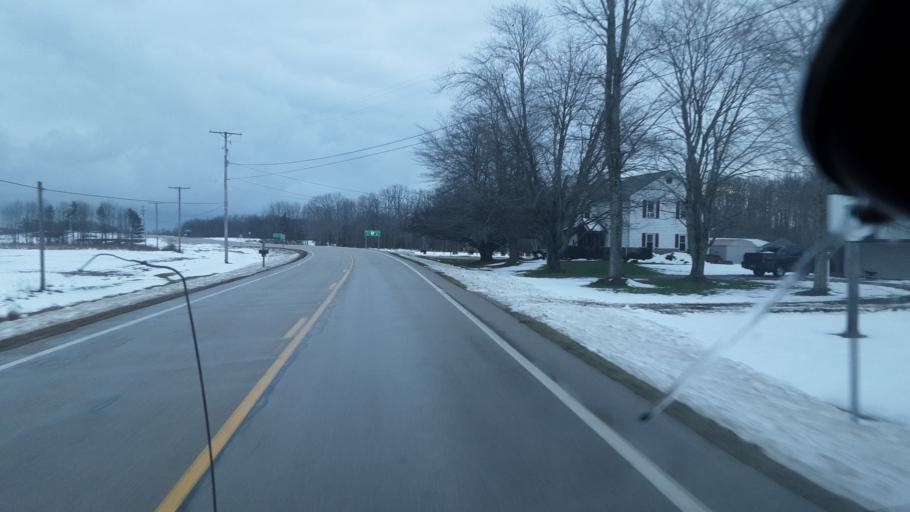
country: US
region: Ohio
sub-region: Ashtabula County
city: Jefferson
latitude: 41.7050
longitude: -80.7163
